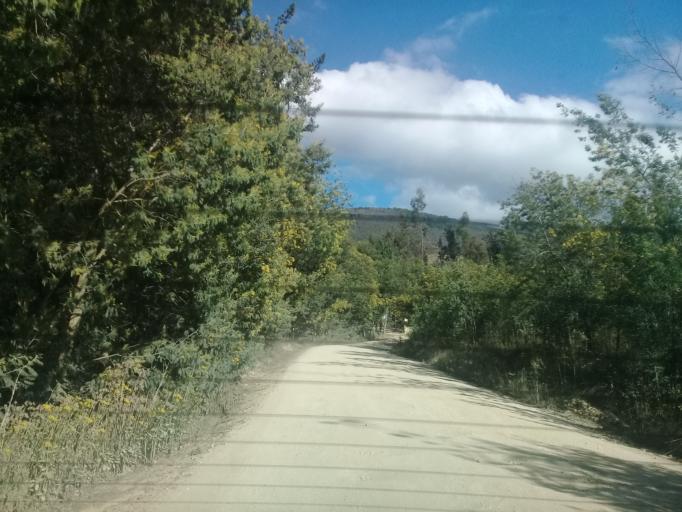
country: CO
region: Cundinamarca
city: Tocancipa
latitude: 4.9301
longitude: -73.8813
